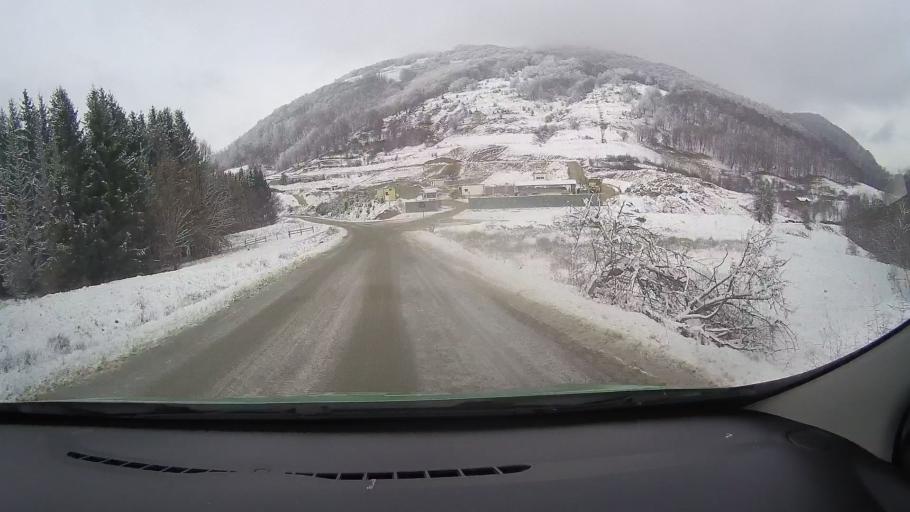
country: RO
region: Alba
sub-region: Comuna Almasu Mare
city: Almasu Mare
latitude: 46.0978
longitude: 23.1588
